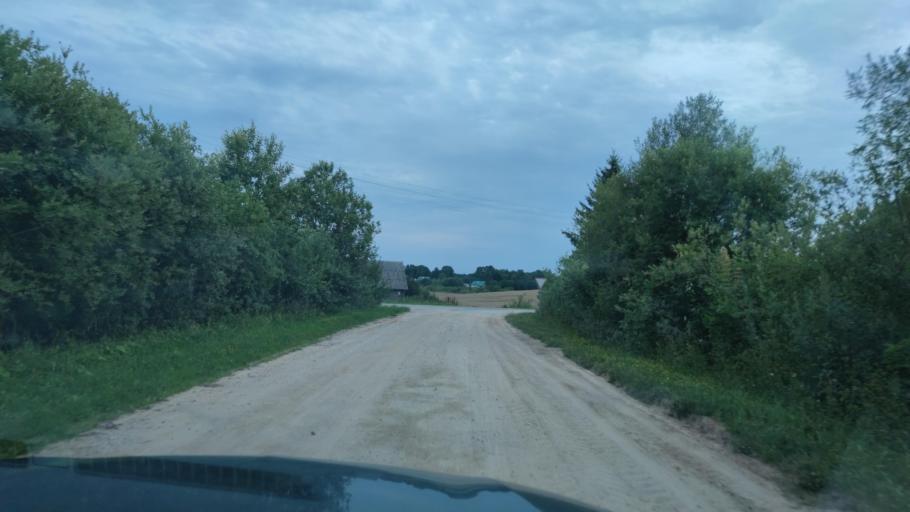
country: BY
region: Minsk
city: Myadzyel
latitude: 55.0901
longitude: 27.1293
